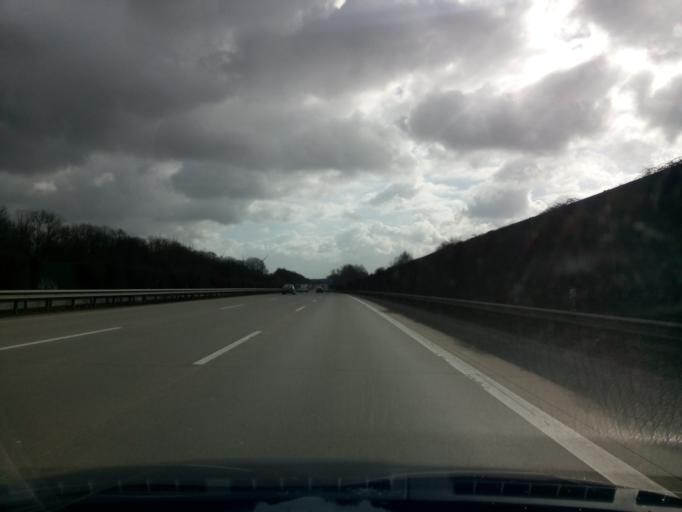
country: DE
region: Lower Saxony
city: Ritterhude
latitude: 53.1308
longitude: 8.7606
